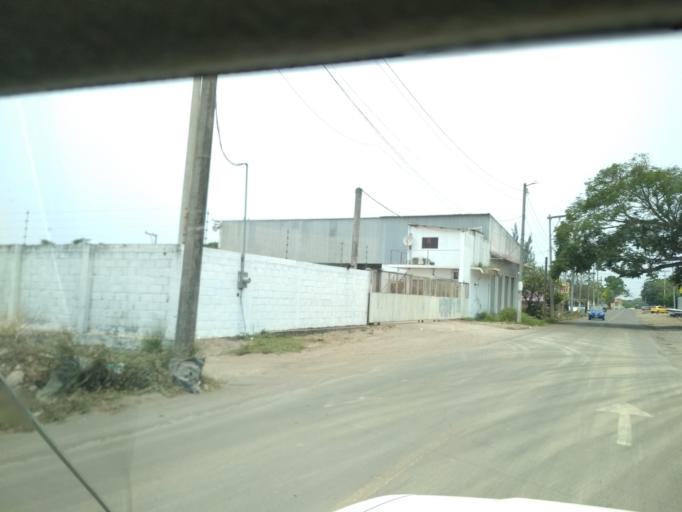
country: MX
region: Veracruz
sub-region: Veracruz
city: Delfino Victoria (Santa Fe)
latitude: 19.2096
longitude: -96.2669
